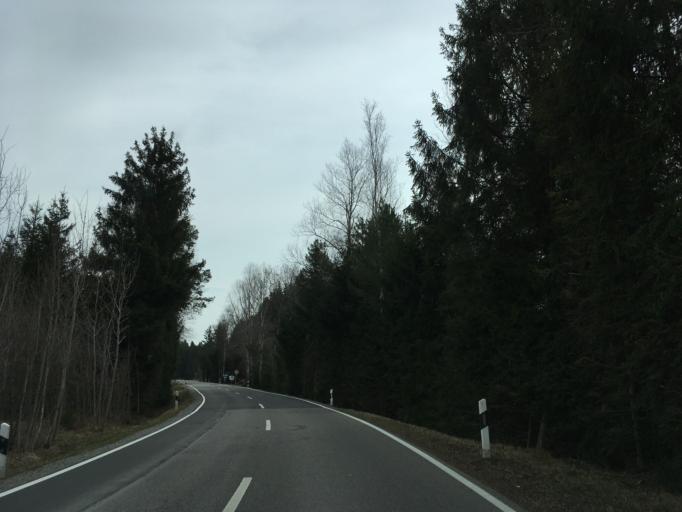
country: DE
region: Bavaria
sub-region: Upper Bavaria
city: Eggstatt
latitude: 47.9490
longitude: 12.4144
